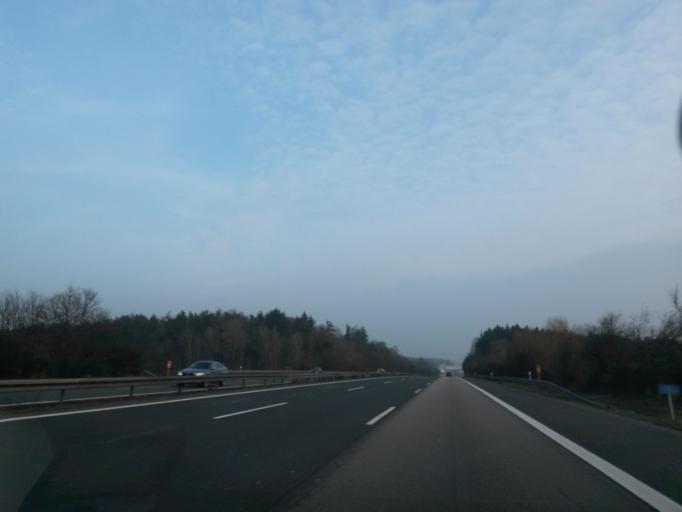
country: DE
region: Bavaria
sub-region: Upper Bavaria
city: Denkendorf
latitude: 48.9429
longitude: 11.4457
